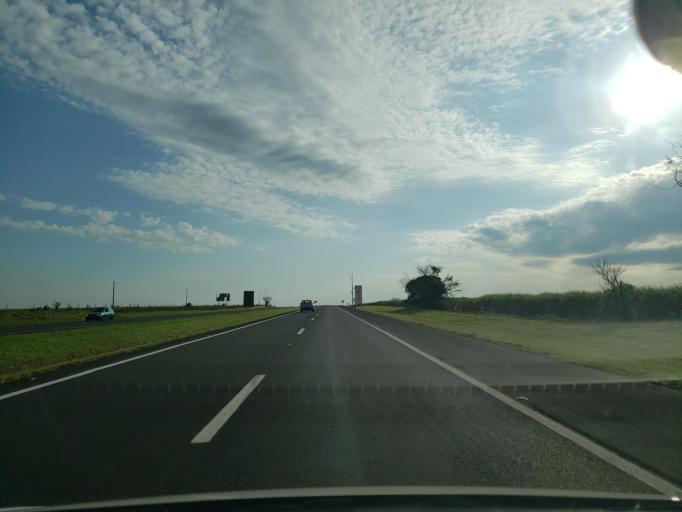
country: BR
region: Sao Paulo
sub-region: Valparaiso
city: Valparaiso
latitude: -21.2046
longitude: -50.8008
